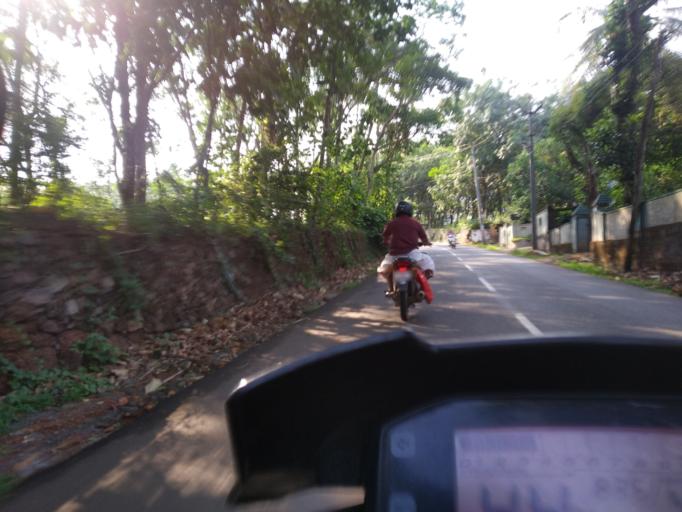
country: IN
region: Kerala
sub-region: Ernakulam
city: Ramamangalam
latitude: 9.9131
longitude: 76.4253
